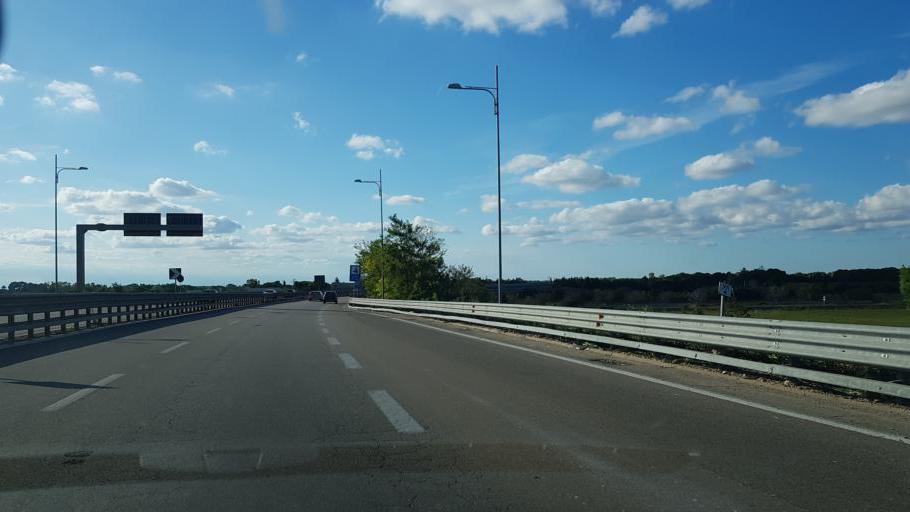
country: IT
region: Apulia
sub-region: Provincia di Lecce
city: Lequile
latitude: 40.3264
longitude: 18.1466
